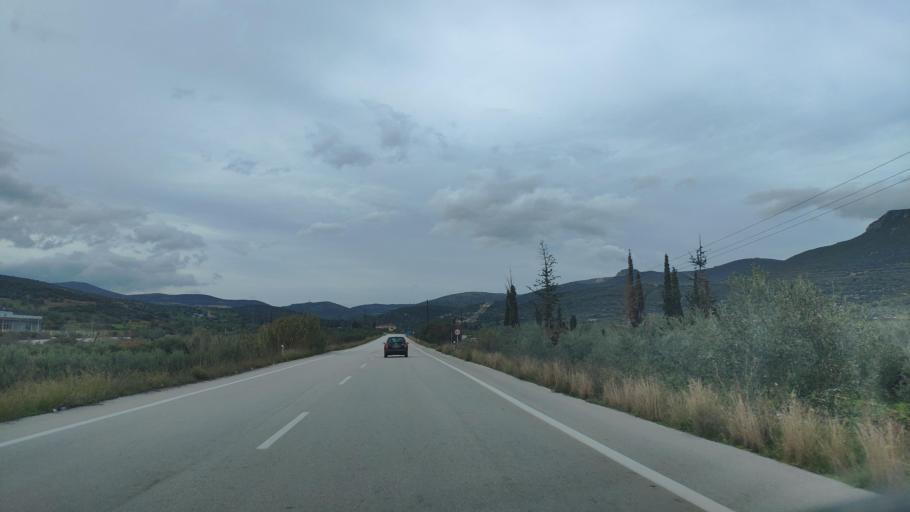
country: GR
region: Peloponnese
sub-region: Nomos Argolidos
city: Koutsopodi
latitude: 37.7486
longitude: 22.7359
